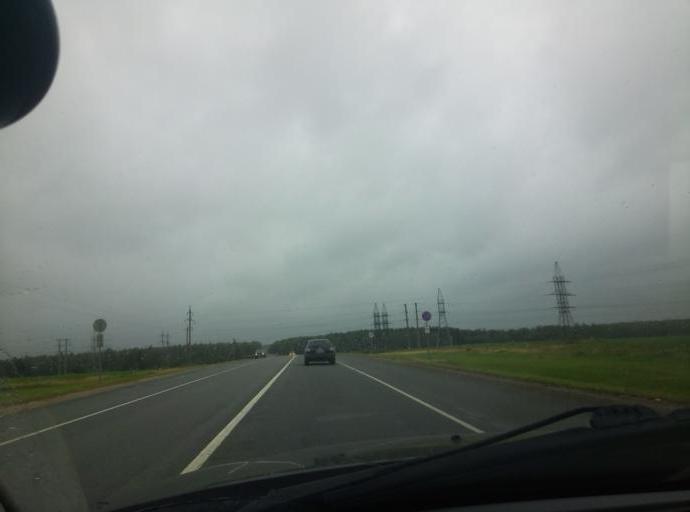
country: RU
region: Tula
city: Barsuki
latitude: 54.2611
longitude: 37.5318
